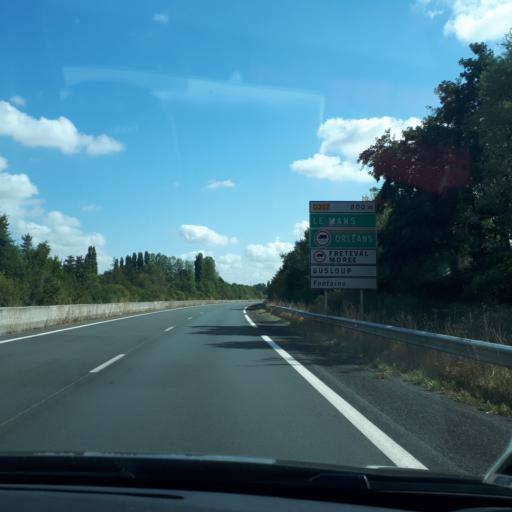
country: FR
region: Centre
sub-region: Departement du Loir-et-Cher
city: Moree
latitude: 47.8855
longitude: 1.1700
